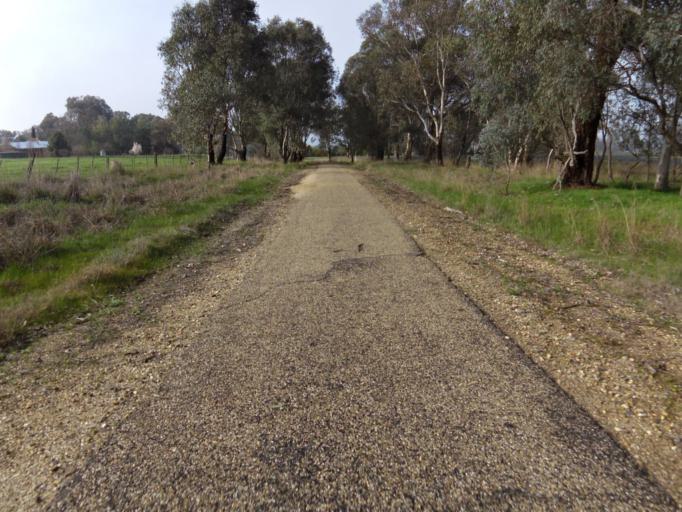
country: AU
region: Victoria
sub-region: Wangaratta
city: Wangaratta
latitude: -36.4521
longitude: 146.5534
